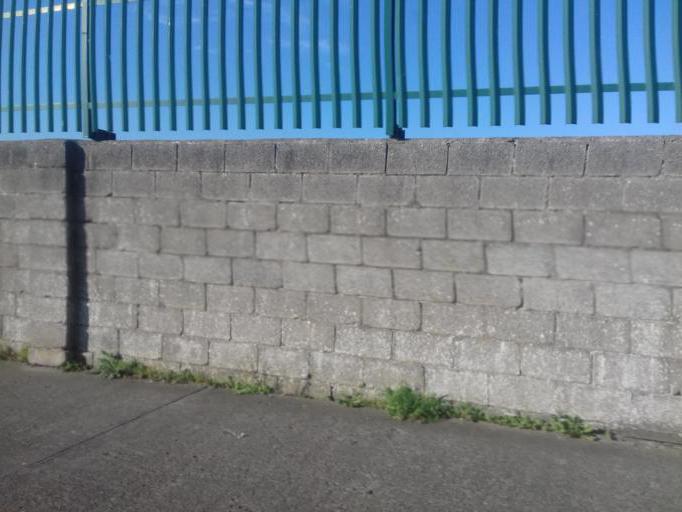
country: IE
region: Leinster
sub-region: Dublin City
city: Finglas
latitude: 53.3835
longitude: -6.3165
